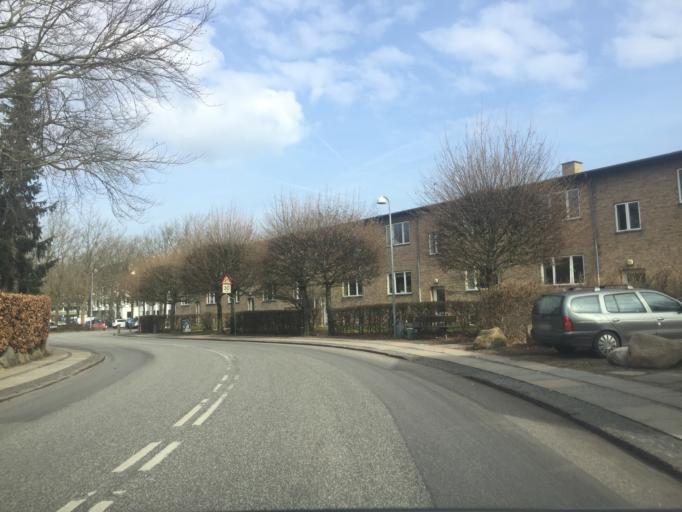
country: DK
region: Capital Region
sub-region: Lyngby-Tarbaek Kommune
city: Kongens Lyngby
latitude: 55.7929
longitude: 12.5049
